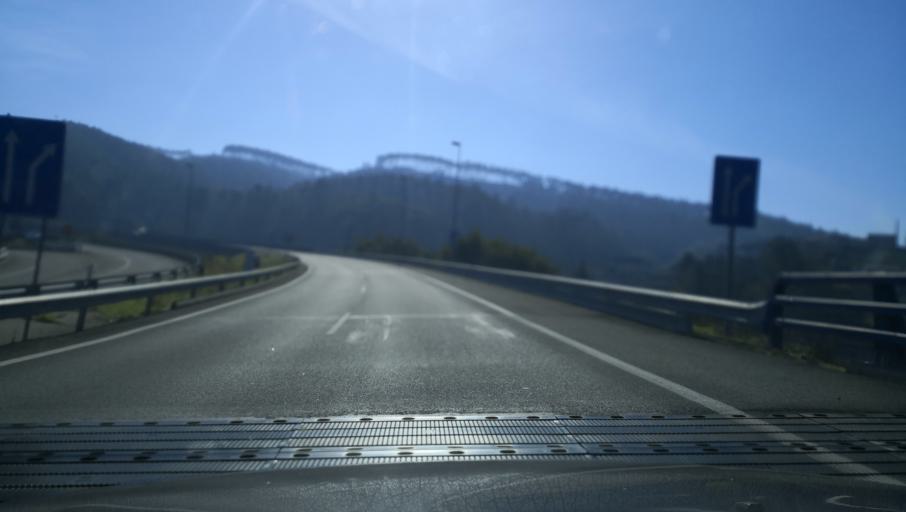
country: ES
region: Galicia
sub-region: Provincia de Ourense
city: Punxin
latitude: 42.3422
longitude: -7.9964
